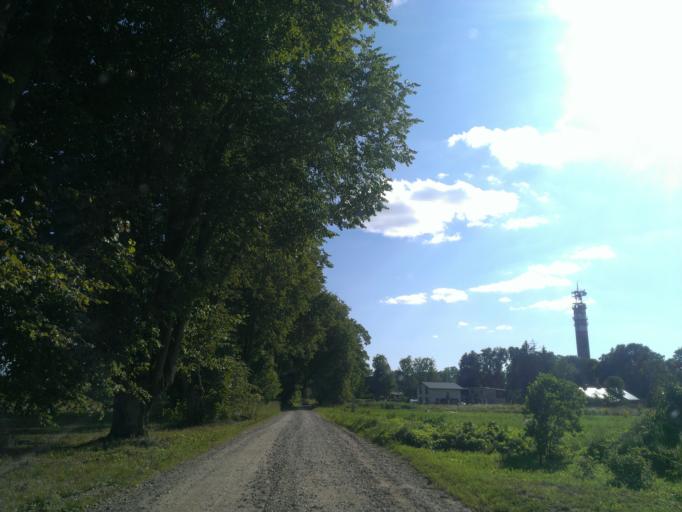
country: LV
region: Sigulda
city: Sigulda
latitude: 57.1669
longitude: 24.8879
